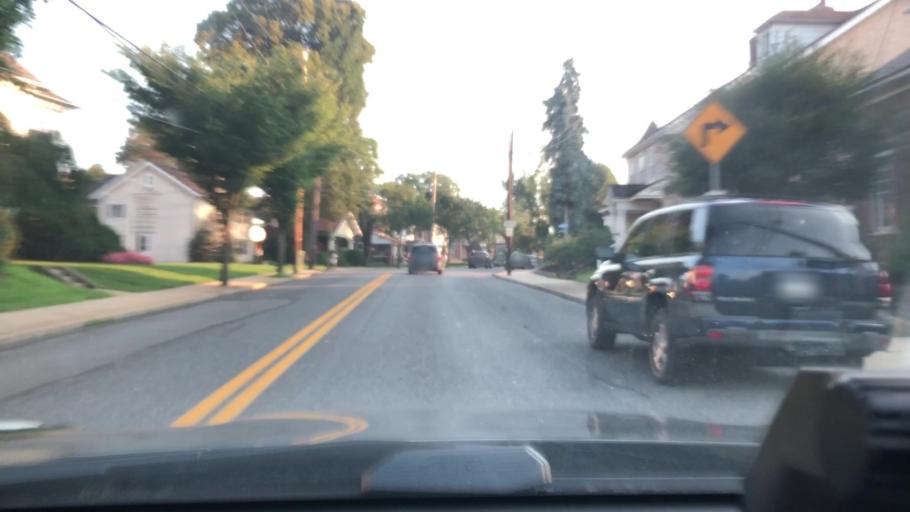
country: US
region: Pennsylvania
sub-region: Lehigh County
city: Emmaus
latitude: 40.5391
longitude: -75.4875
